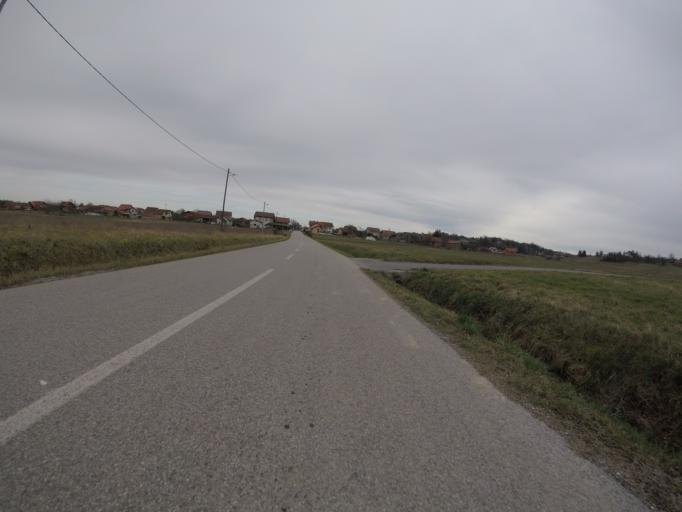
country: HR
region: Grad Zagreb
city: Strmec
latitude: 45.6661
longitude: 15.9347
